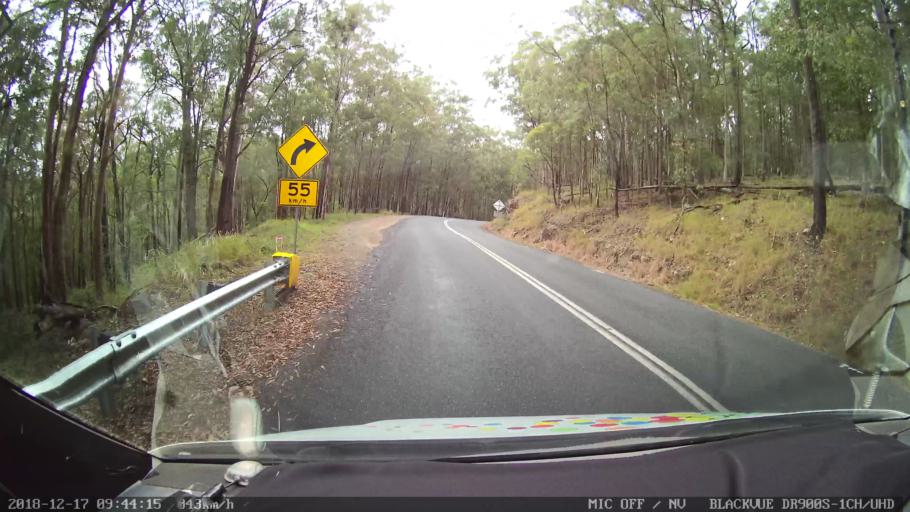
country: AU
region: New South Wales
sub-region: Tenterfield Municipality
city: Carrolls Creek
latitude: -28.9249
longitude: 152.3243
